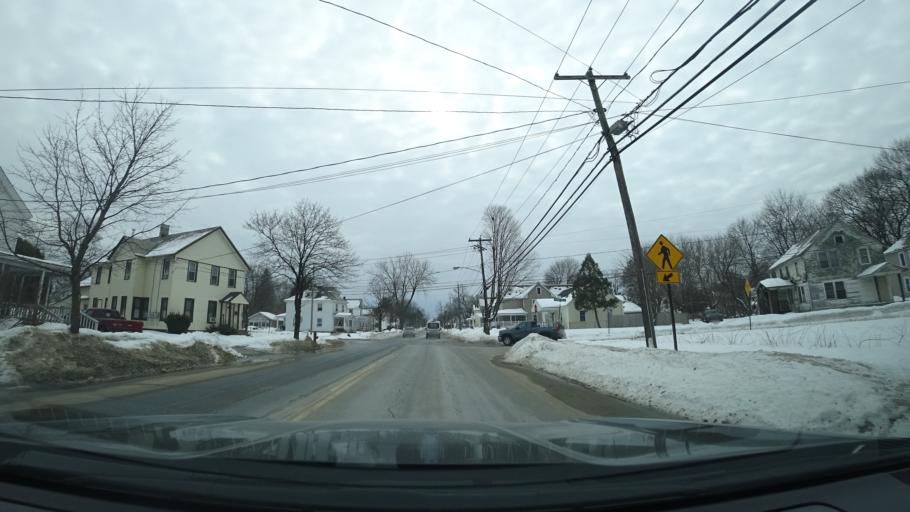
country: US
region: New York
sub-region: Saratoga County
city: South Glens Falls
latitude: 43.2966
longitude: -73.6329
